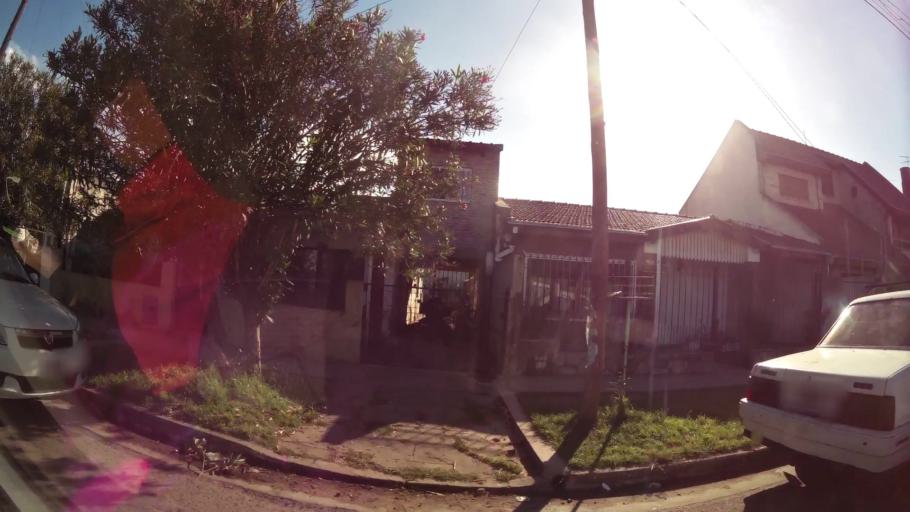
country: AR
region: Buenos Aires
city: Santa Catalina - Dique Lujan
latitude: -34.4916
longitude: -58.7262
